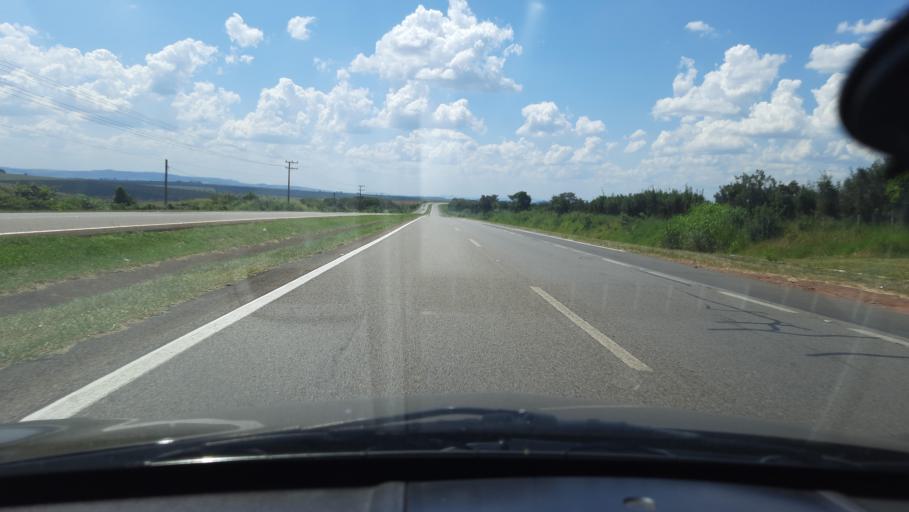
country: BR
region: Sao Paulo
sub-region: Casa Branca
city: Casa Branca
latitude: -21.7188
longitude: -47.0809
